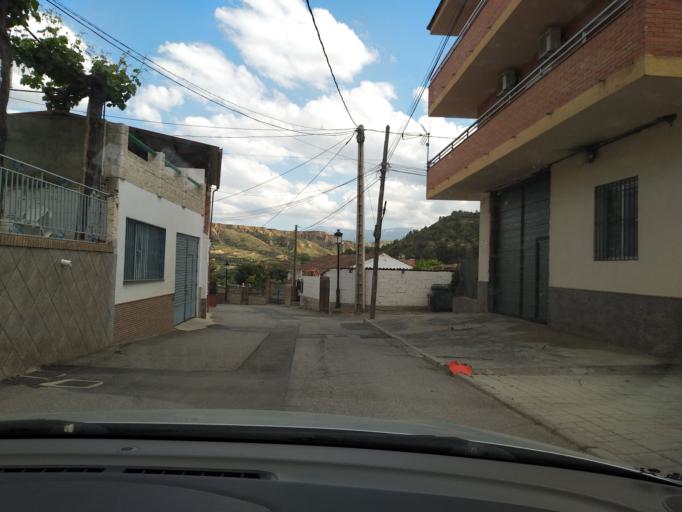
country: ES
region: Andalusia
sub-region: Provincia de Granada
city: Marchal
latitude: 37.2962
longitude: -3.2041
